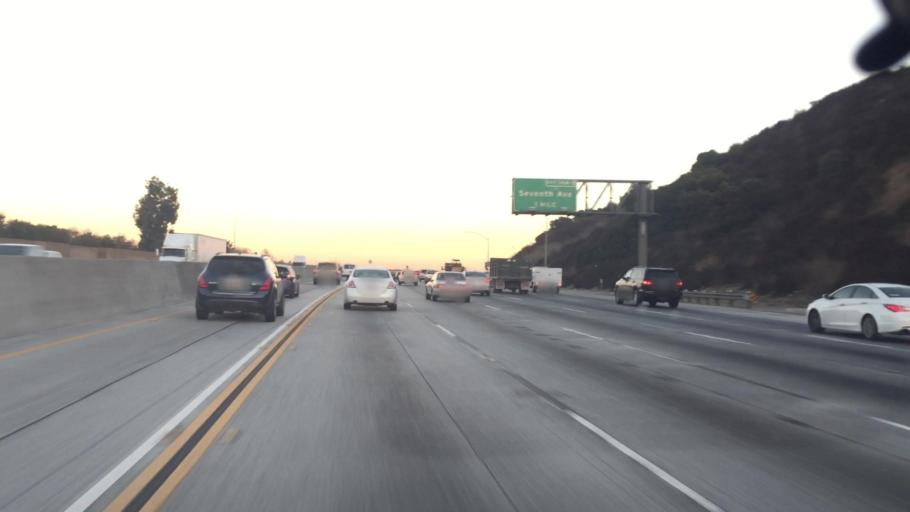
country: US
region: California
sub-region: Los Angeles County
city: Avocado Heights
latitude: 34.0290
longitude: -118.0048
